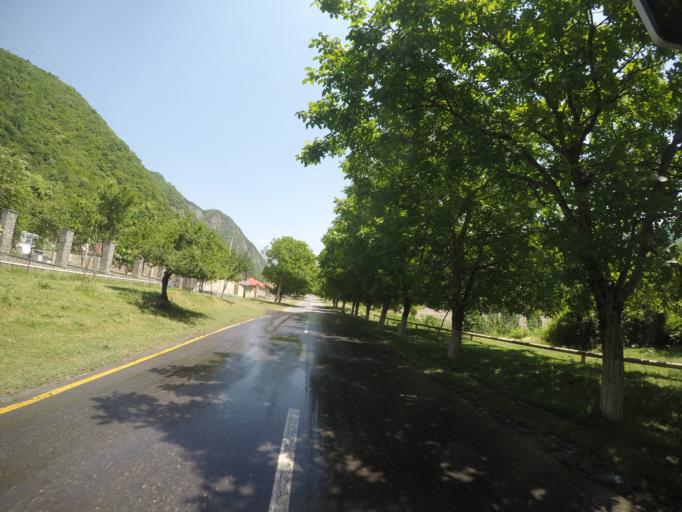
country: AZ
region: Qakh Rayon
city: Qaxbas
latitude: 41.4494
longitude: 47.0024
